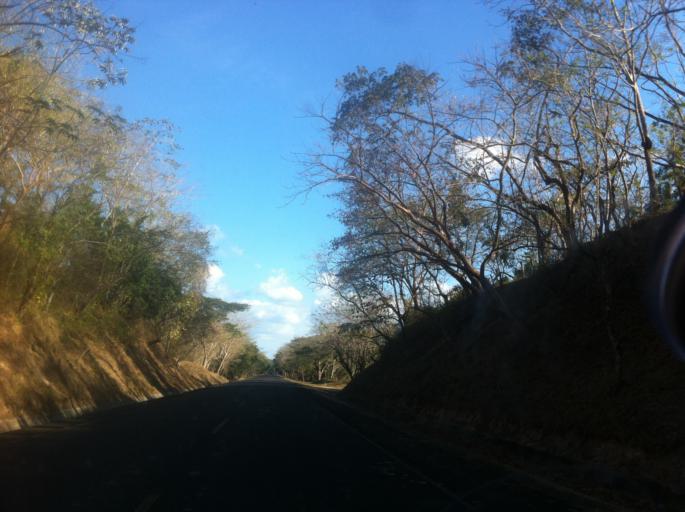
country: NI
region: Rio San Juan
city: Morrito
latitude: 11.7171
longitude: -84.9603
